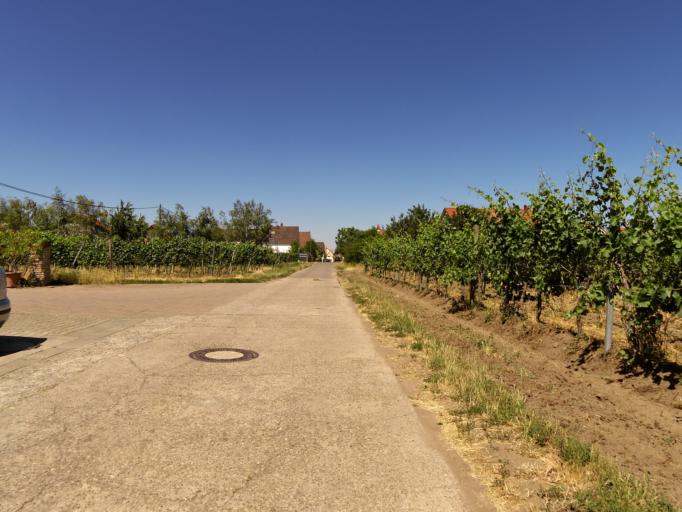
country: DE
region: Rheinland-Pfalz
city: Neustadt
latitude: 49.3632
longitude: 8.1711
